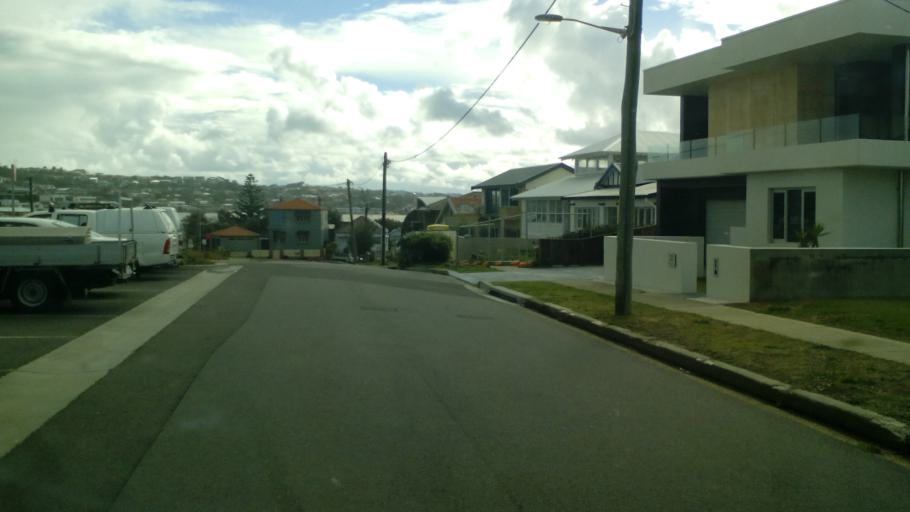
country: AU
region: New South Wales
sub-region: Newcastle
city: Bar Beach
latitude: -32.9441
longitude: 151.7611
